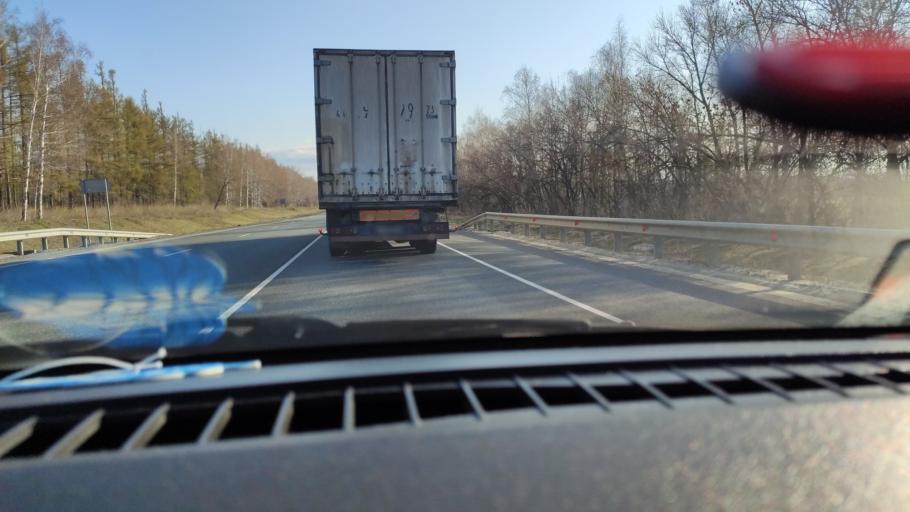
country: RU
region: Saratov
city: Khvalynsk
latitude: 52.5695
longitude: 48.1001
